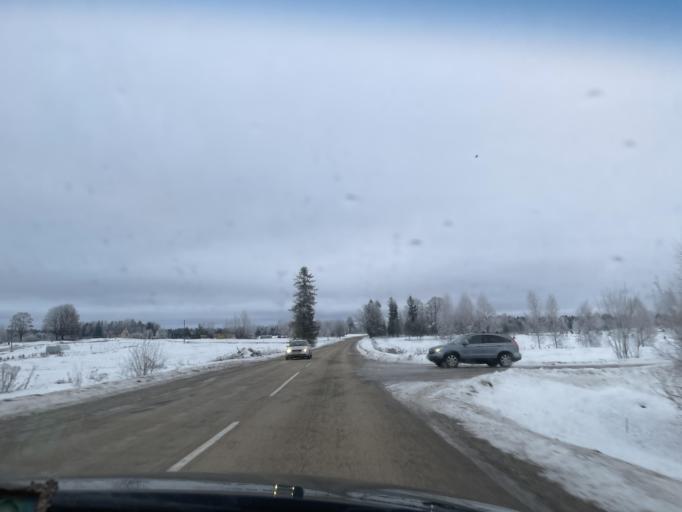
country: LV
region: Rezekne
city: Rezekne
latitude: 56.4971
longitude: 27.4098
